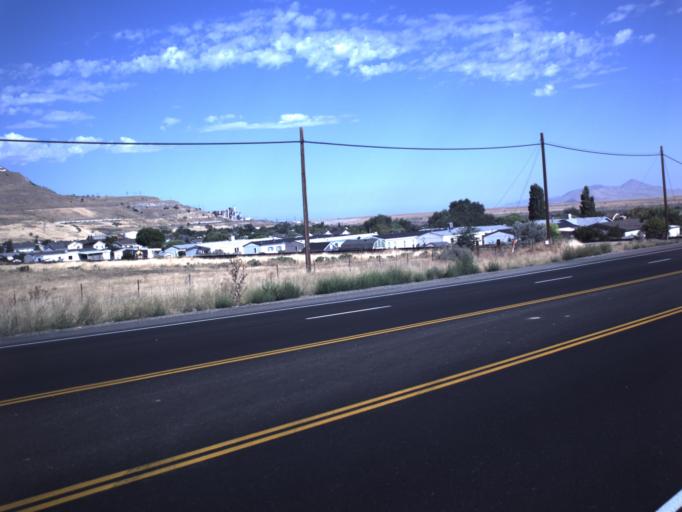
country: US
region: Utah
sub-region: Salt Lake County
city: Magna
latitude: 40.6882
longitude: -112.0918
